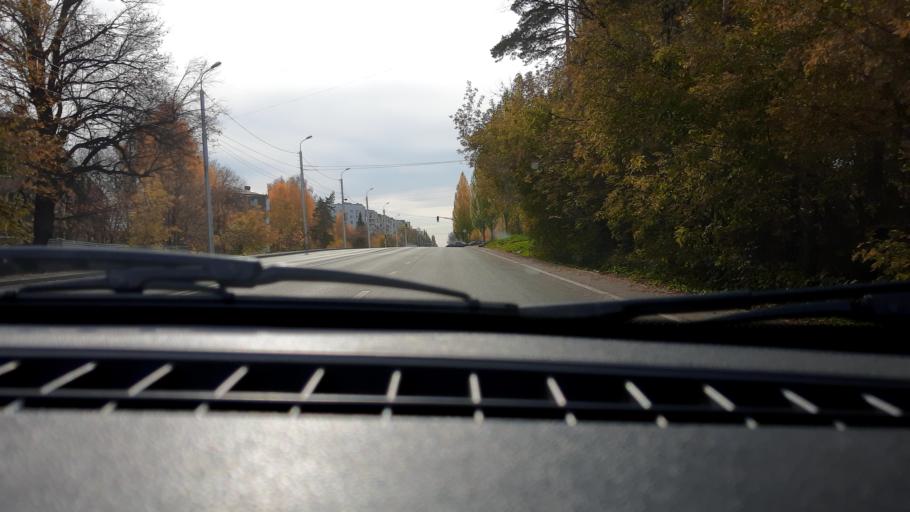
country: RU
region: Bashkortostan
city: Ufa
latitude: 54.7951
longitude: 56.0434
